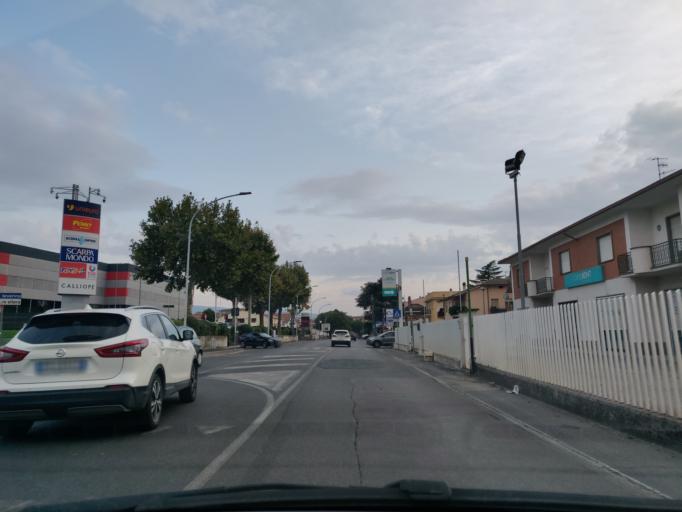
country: IT
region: Latium
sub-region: Provincia di Viterbo
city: Viterbo
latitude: 42.4313
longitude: 12.0999
